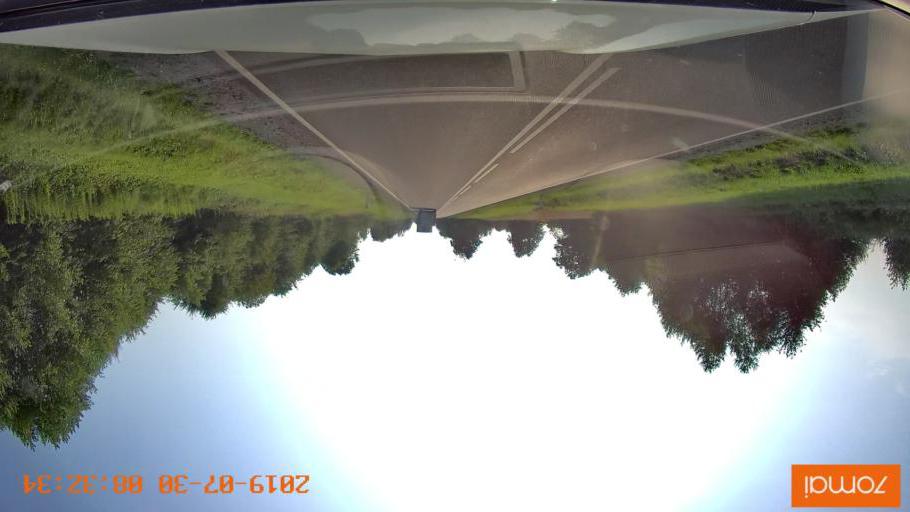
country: RU
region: Kaliningrad
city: Chernyakhovsk
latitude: 54.6375
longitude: 21.7307
